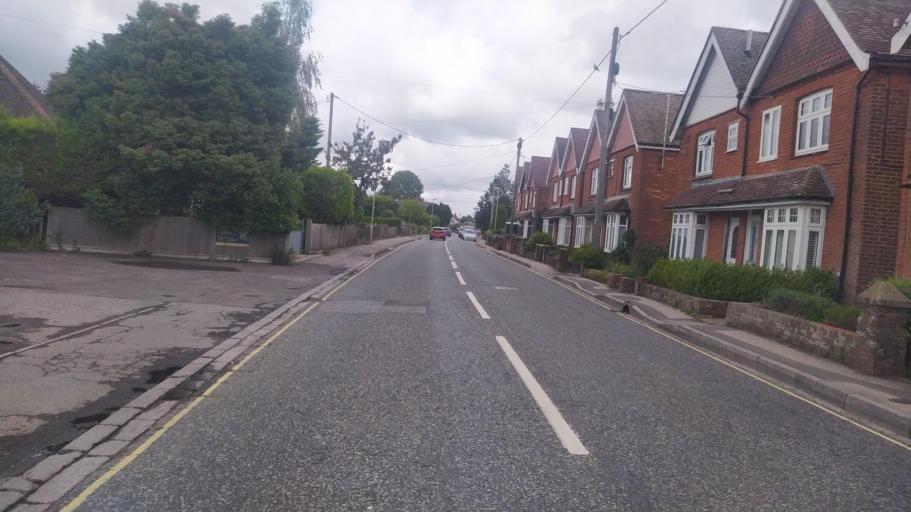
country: GB
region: England
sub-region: Hampshire
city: Liphook
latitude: 51.0782
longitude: -0.8038
